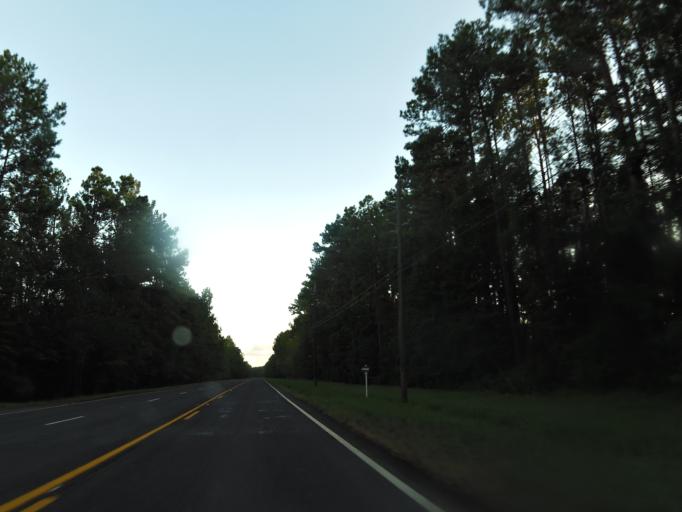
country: US
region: Georgia
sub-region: Camden County
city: Woodbine
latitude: 31.0142
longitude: -81.7315
